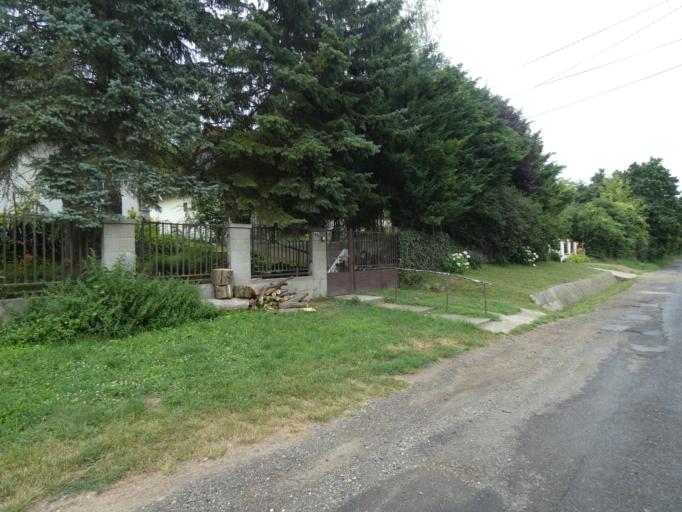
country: HU
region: Pest
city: Szob
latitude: 47.8126
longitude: 18.9014
